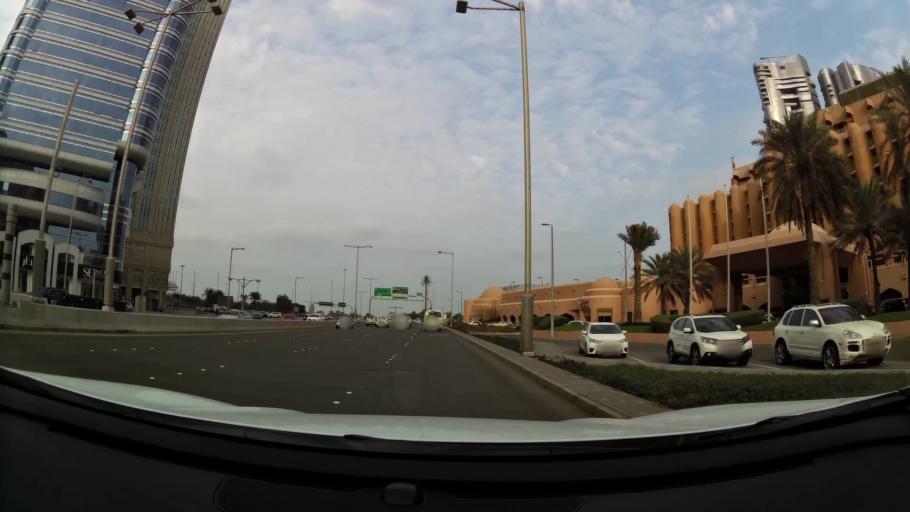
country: AE
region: Abu Dhabi
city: Abu Dhabi
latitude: 24.4998
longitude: 54.3687
